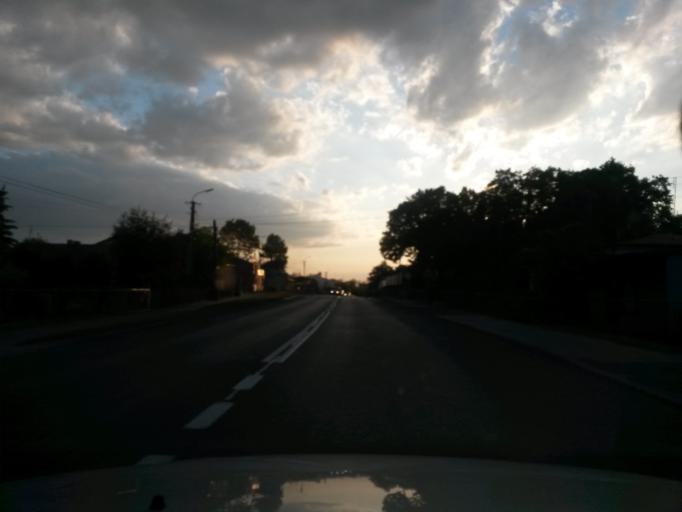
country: PL
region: Lodz Voivodeship
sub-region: Powiat wieruszowski
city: Walichnowy
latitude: 51.2659
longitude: 18.4507
